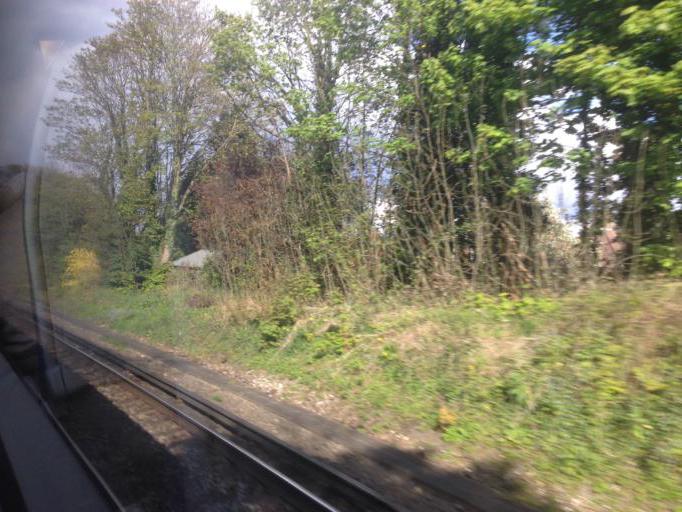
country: GB
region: England
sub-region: Greater London
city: Carshalton
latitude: 51.3641
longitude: -0.1732
